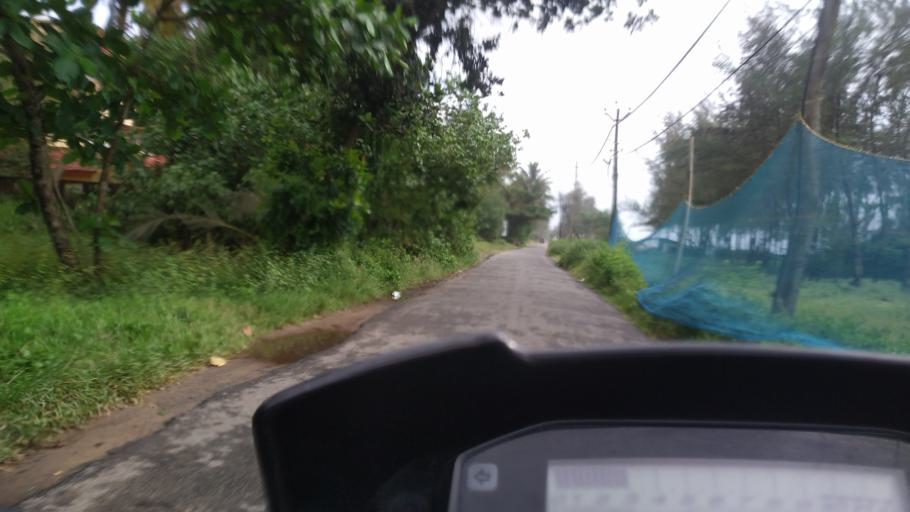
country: IN
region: Kerala
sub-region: Thrissur District
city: Kodungallur
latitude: 10.1510
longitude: 76.1755
